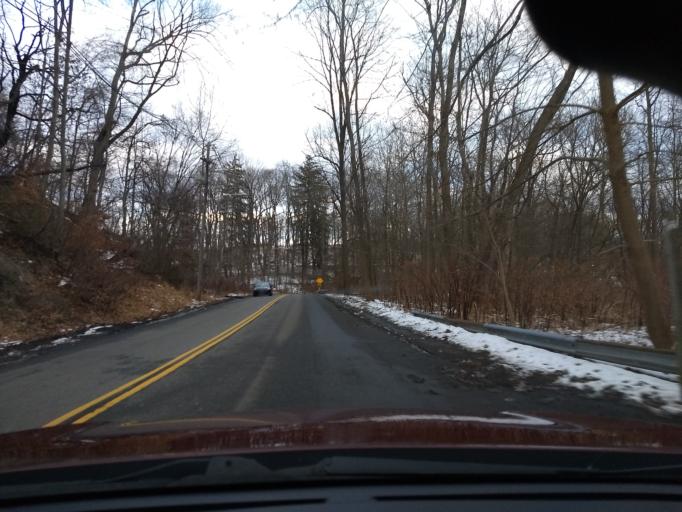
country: US
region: New Jersey
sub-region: Morris County
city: Morris Plains
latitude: 40.8128
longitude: -74.4798
